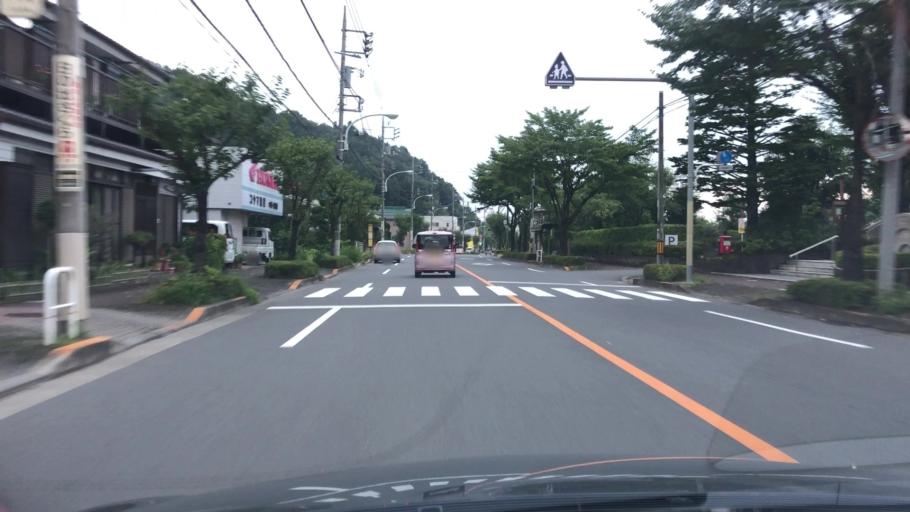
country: JP
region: Tokyo
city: Itsukaichi
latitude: 35.7427
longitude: 139.2574
